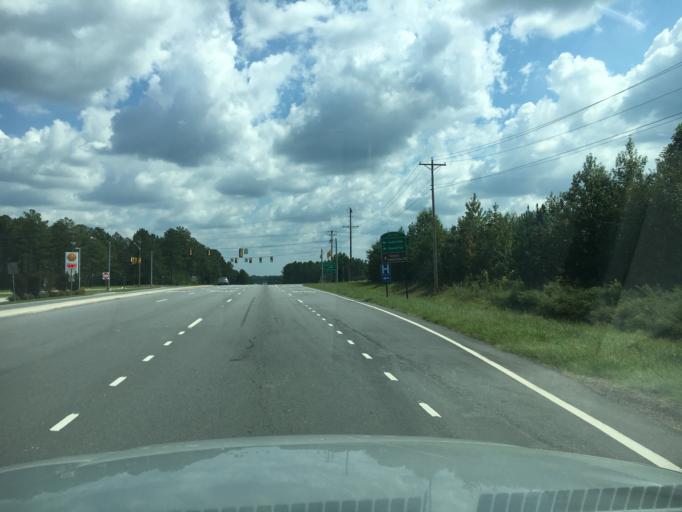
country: US
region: South Carolina
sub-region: Greenwood County
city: Greenwood
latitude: 34.1589
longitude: -82.1773
